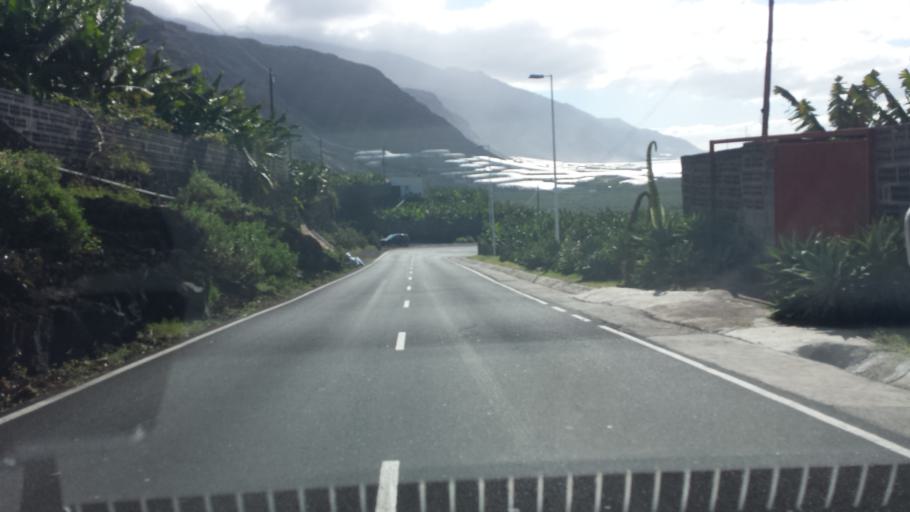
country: ES
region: Canary Islands
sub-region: Provincia de Santa Cruz de Tenerife
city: Tazacorte
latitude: 28.5905
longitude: -17.9101
